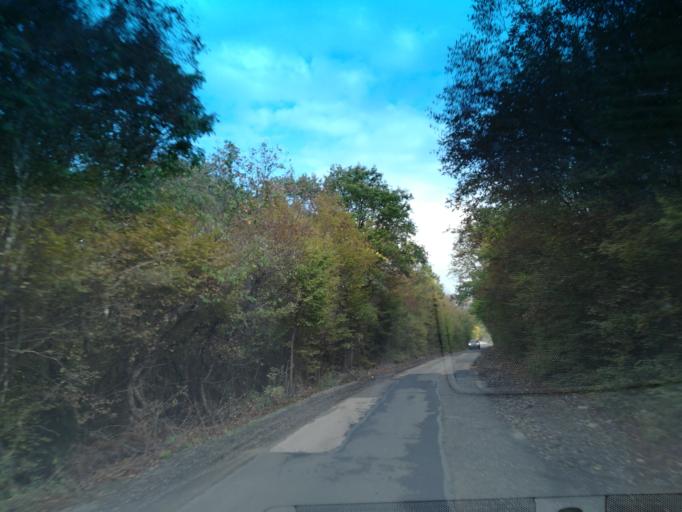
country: BG
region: Stara Zagora
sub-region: Obshtina Nikolaevo
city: Elkhovo
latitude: 42.3259
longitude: 25.3989
